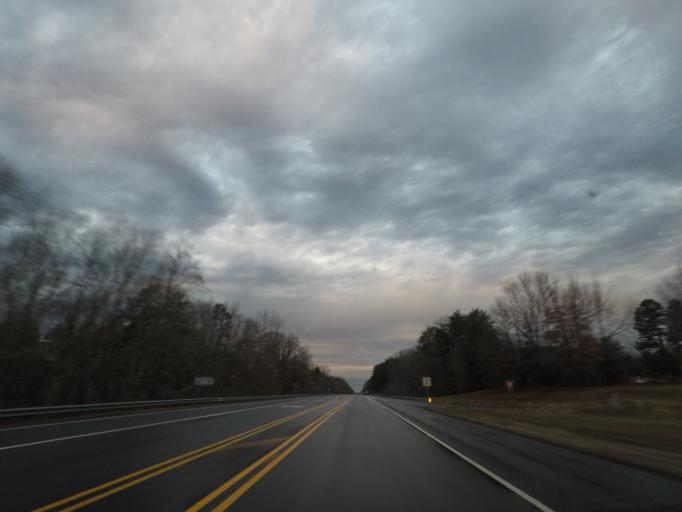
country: US
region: North Carolina
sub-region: Caswell County
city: Yanceyville
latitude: 36.3882
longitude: -79.2727
